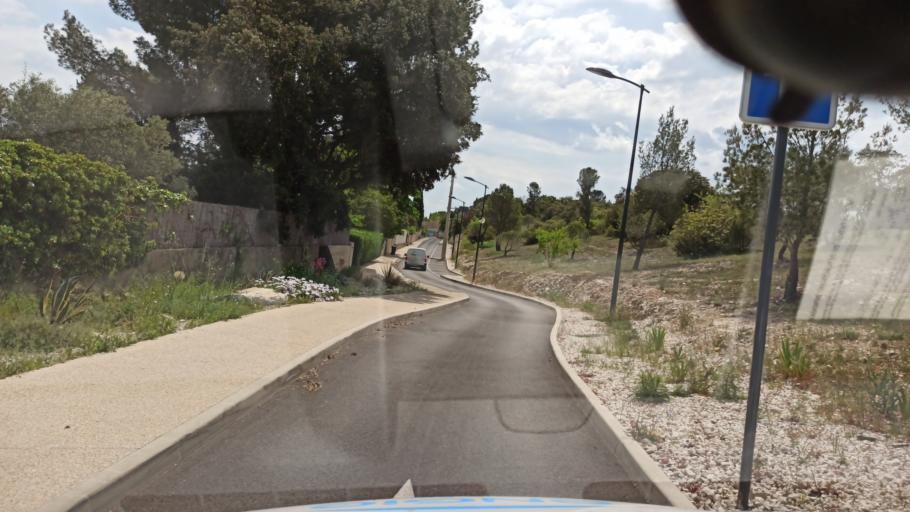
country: FR
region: Languedoc-Roussillon
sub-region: Departement du Gard
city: Les Angles
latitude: 43.9639
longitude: 4.7754
